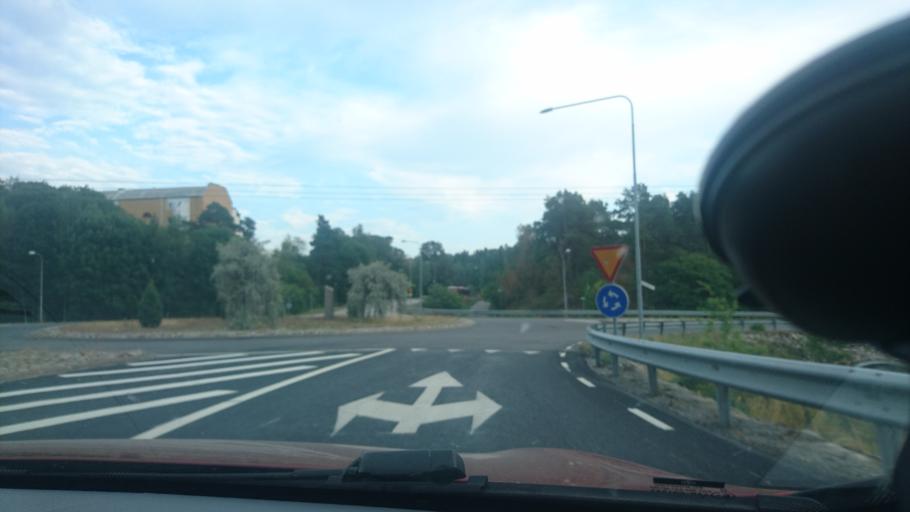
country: SE
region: Stockholm
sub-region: Upplands Vasby Kommun
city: Upplands Vaesby
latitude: 59.4986
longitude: 17.9320
